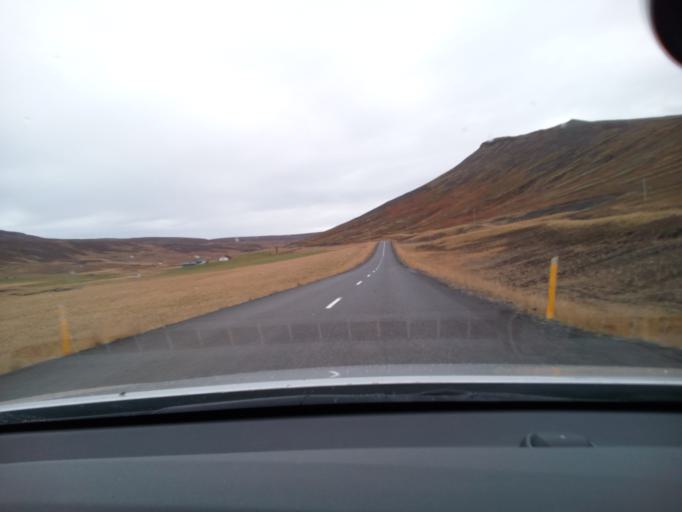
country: IS
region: Northeast
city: Laugar
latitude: 65.8022
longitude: -17.2605
